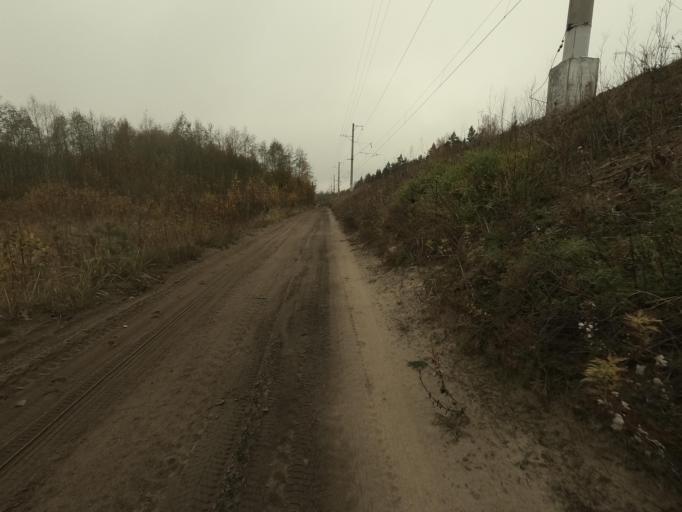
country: RU
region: Leningrad
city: Pavlovo
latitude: 59.7795
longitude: 30.8980
